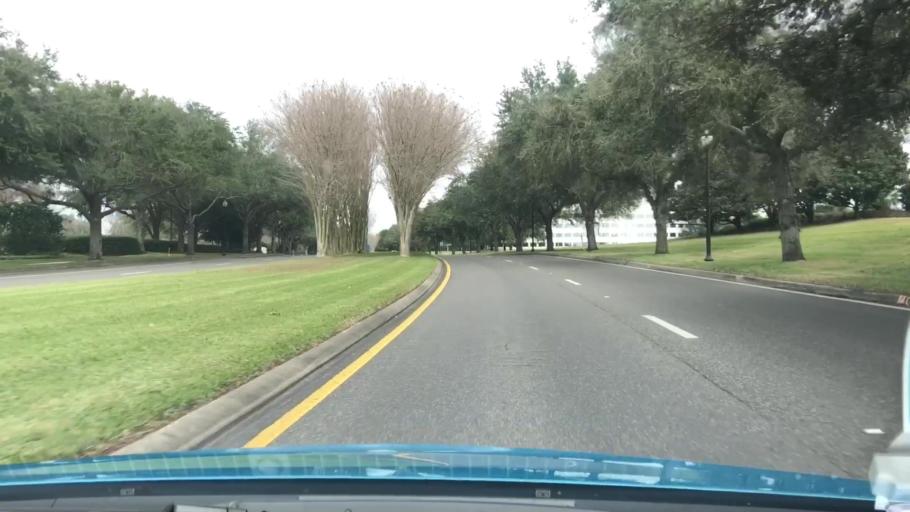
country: US
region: Florida
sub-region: Seminole County
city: Heathrow
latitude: 28.7711
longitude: -81.3588
